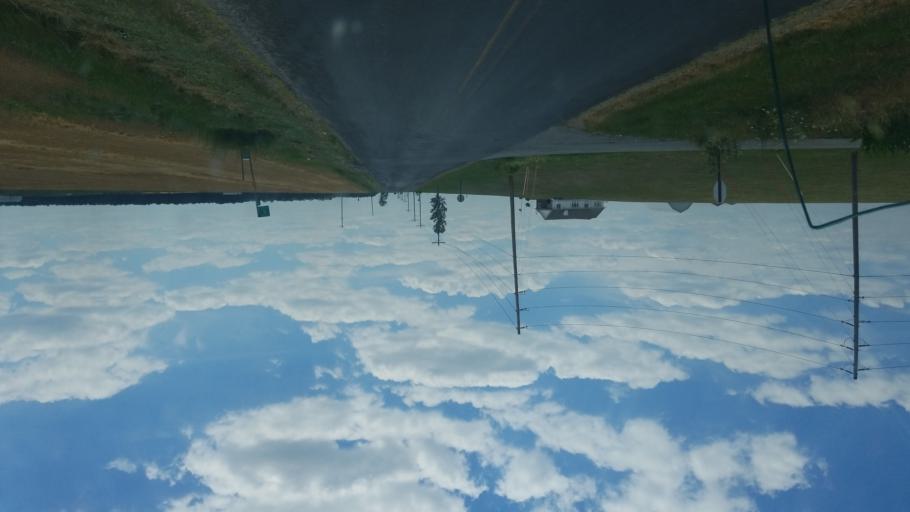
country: US
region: Ohio
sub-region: Williams County
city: Edgerton
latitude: 41.4558
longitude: -84.6912
